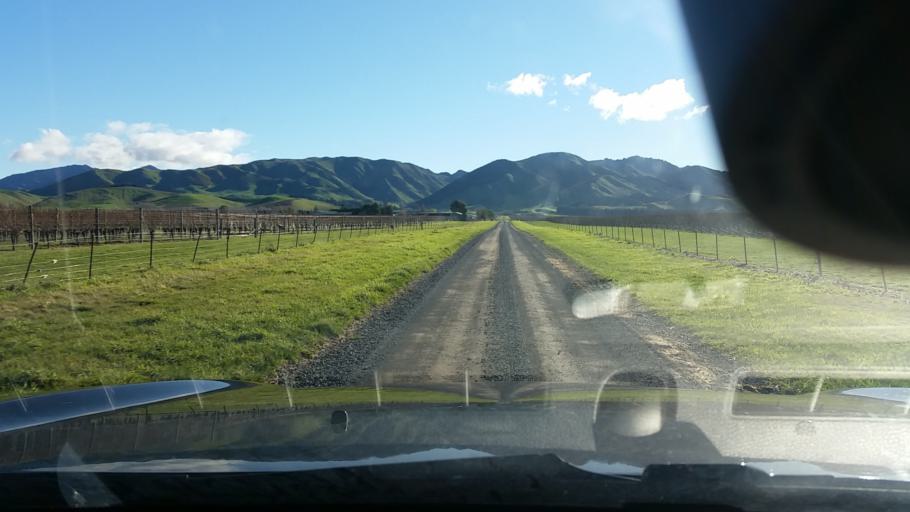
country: NZ
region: Marlborough
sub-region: Marlborough District
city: Blenheim
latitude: -41.6462
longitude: 174.0521
